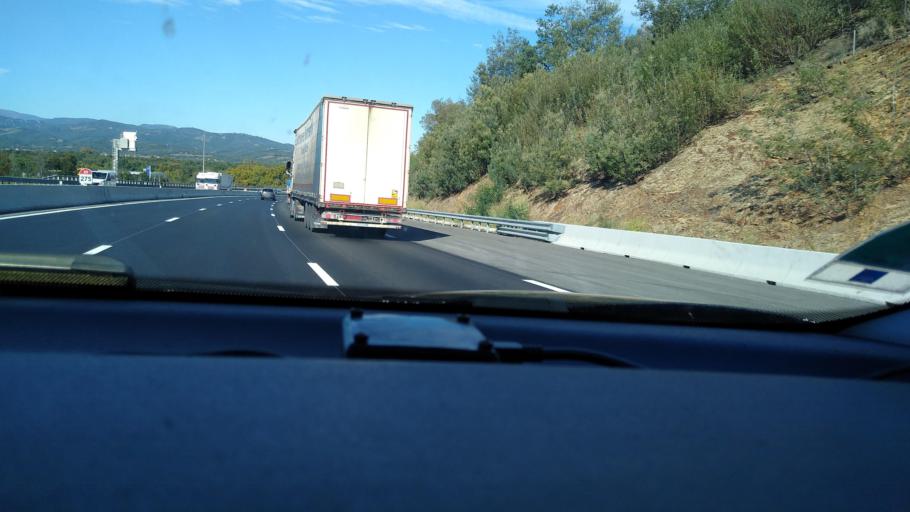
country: FR
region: Languedoc-Roussillon
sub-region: Departement des Pyrenees-Orientales
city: Maureillas-las-Illas
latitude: 42.4980
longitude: 2.8225
